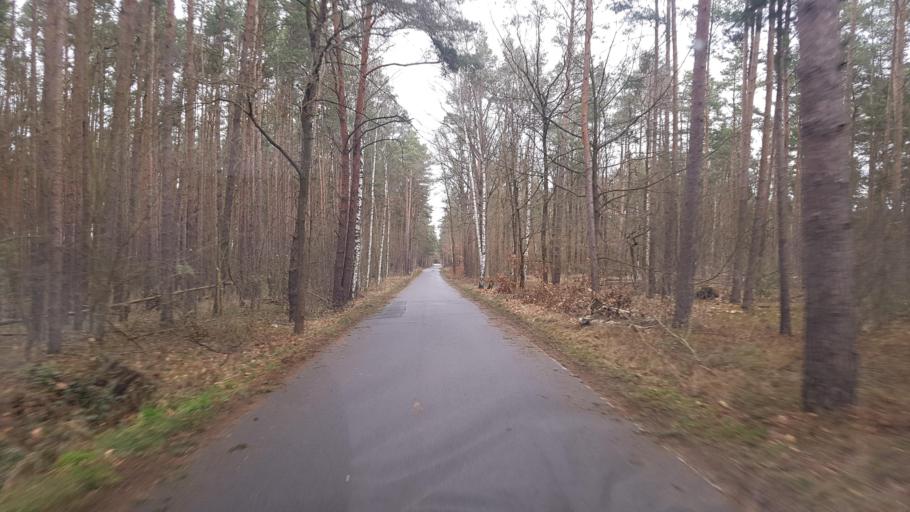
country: DE
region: Brandenburg
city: Kroppen
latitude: 51.3685
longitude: 13.7903
